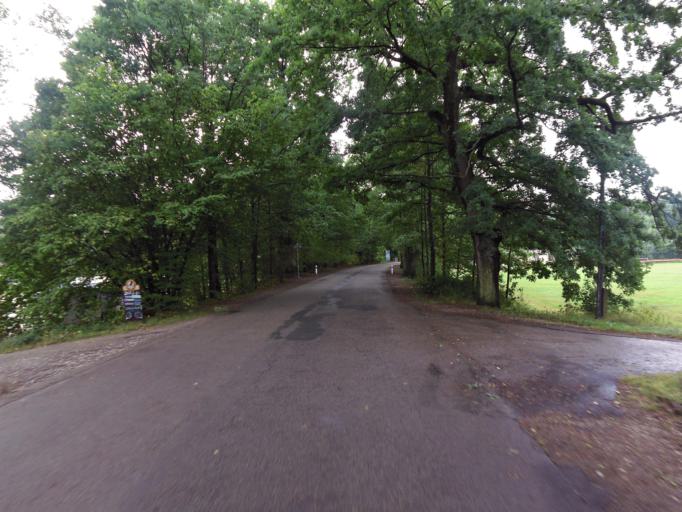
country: CZ
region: Jihocesky
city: Chlum u Trebone
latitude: 48.9759
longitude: 14.9544
